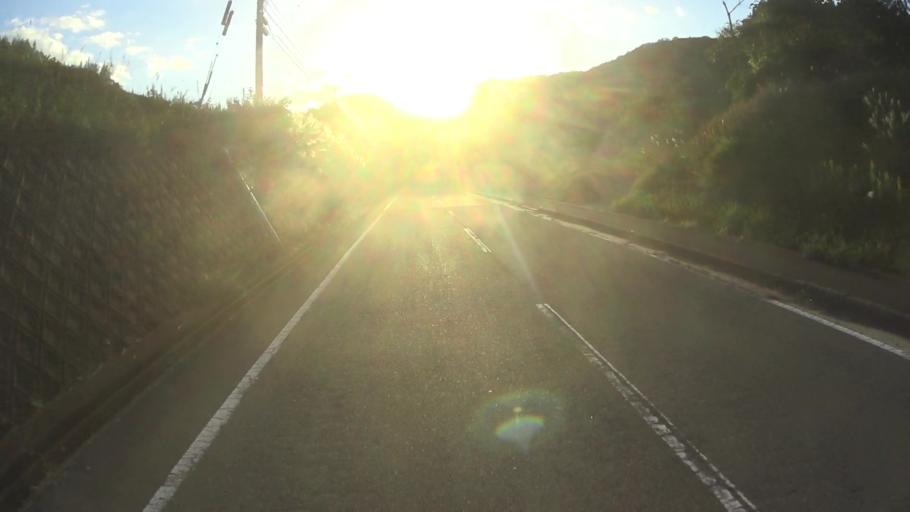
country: JP
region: Kyoto
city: Ayabe
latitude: 35.2306
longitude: 135.2468
